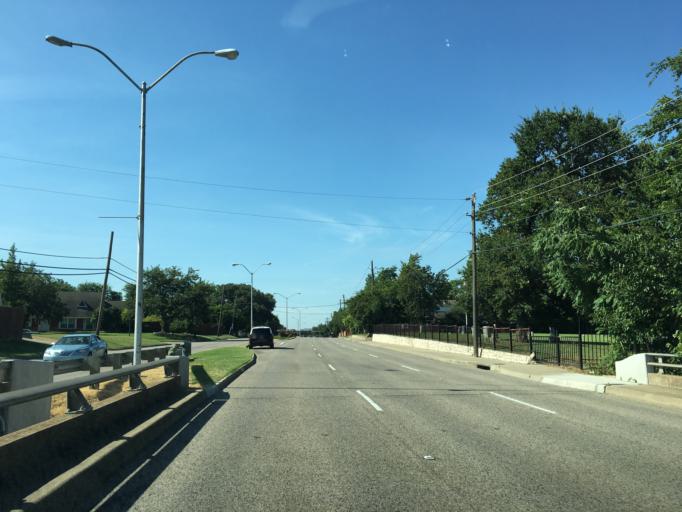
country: US
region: Texas
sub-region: Dallas County
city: Farmers Branch
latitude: 32.9183
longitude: -96.8732
